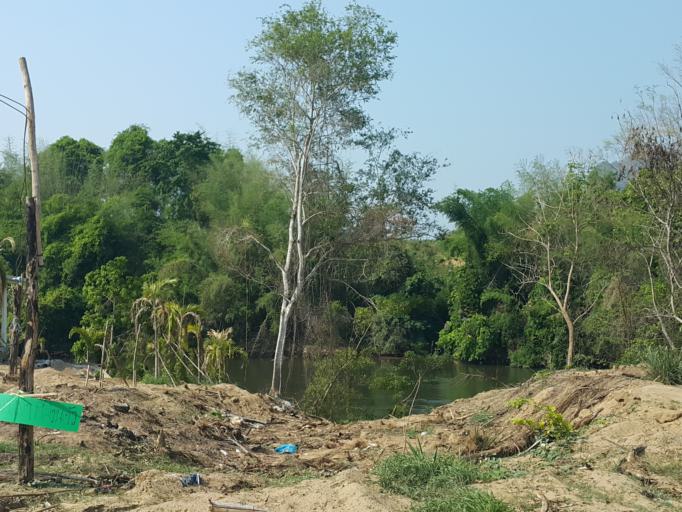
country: TH
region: Kanchanaburi
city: Sai Yok
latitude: 14.1097
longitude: 99.1353
